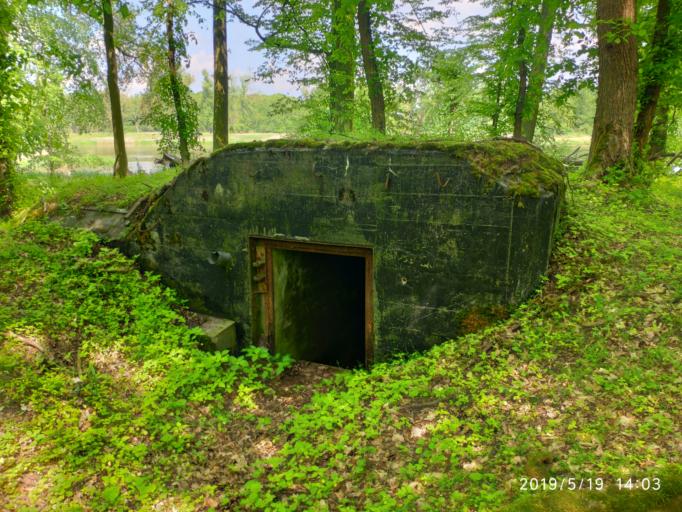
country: PL
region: Lubusz
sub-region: Powiat krosnienski
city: Dabie
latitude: 52.0578
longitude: 15.2766
